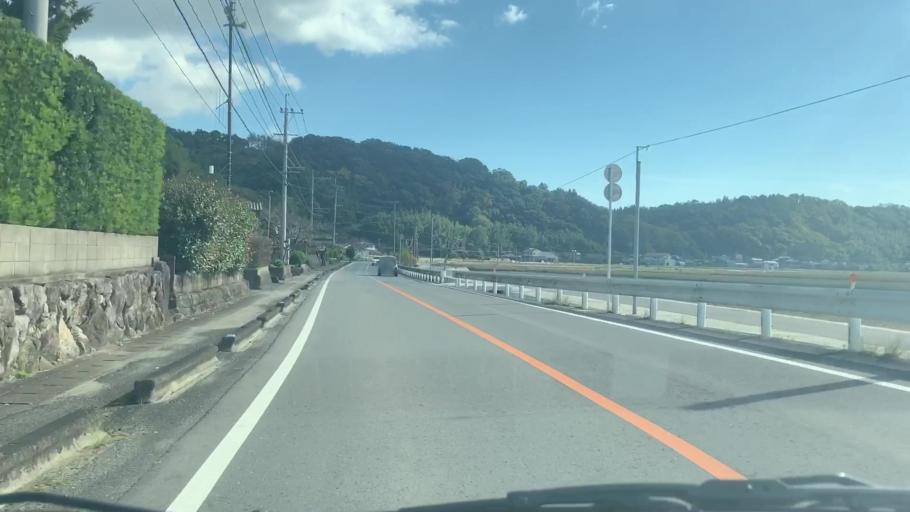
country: JP
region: Saga Prefecture
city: Saga-shi
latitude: 33.2754
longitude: 130.1705
